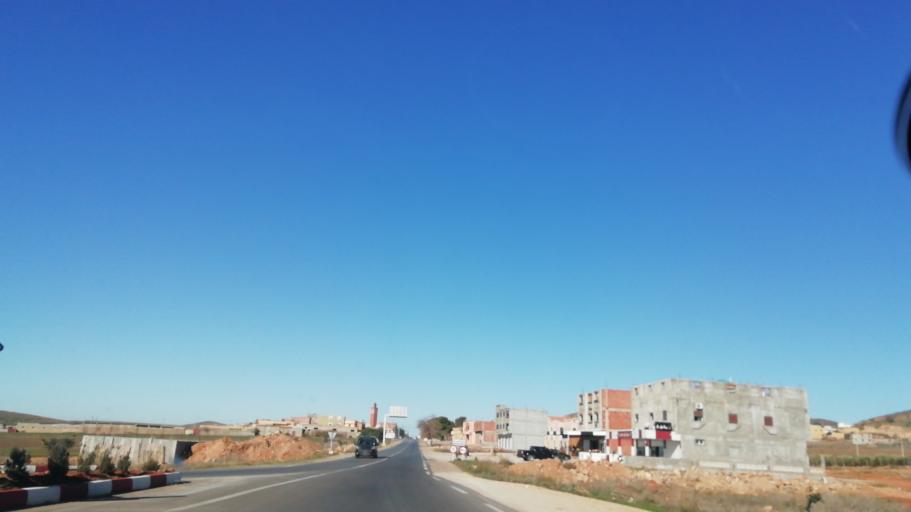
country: DZ
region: Tlemcen
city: Nedroma
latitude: 34.8826
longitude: -1.9018
